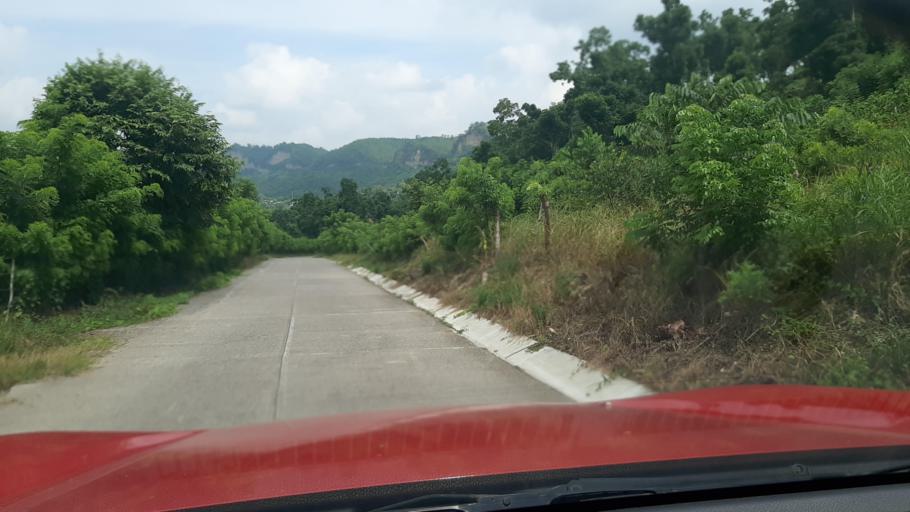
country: MX
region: Veracruz
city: Gutierrez Zamora
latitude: 20.4604
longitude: -97.1838
